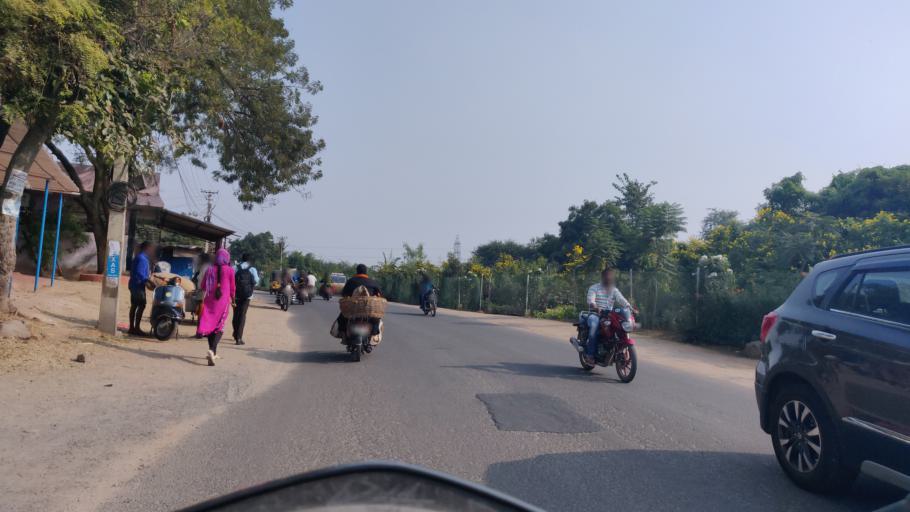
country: IN
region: Telangana
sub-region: Rangareddi
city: Uppal Kalan
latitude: 17.4004
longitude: 78.5827
